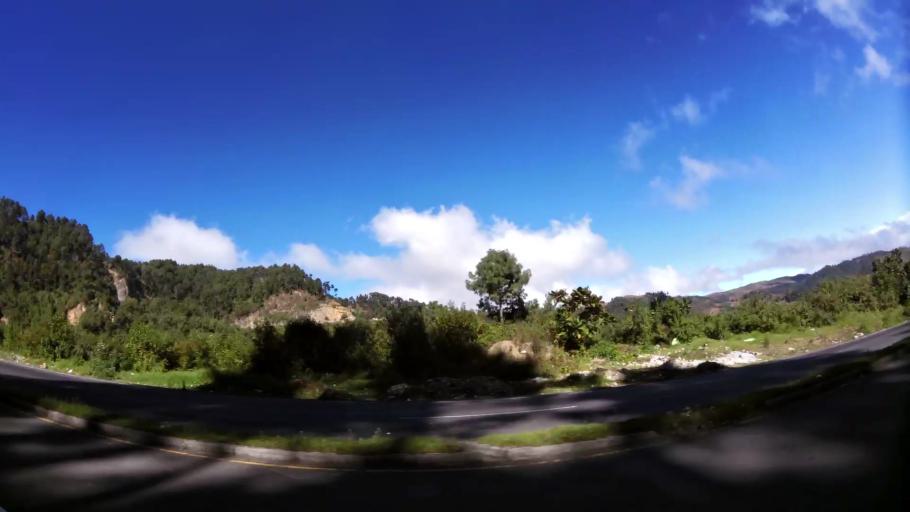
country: GT
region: Solola
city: Santa Catarina Ixtahuacan
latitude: 14.8221
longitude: -91.3471
